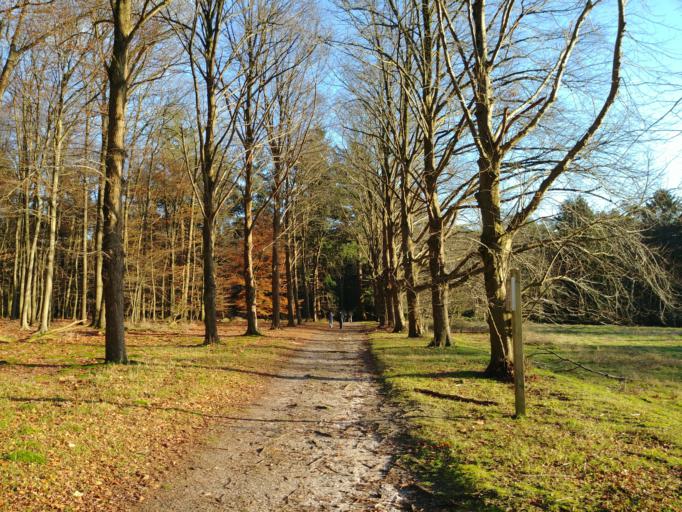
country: NL
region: Utrecht
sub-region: Gemeente Utrechtse Heuvelrug
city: Maarn
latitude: 52.0362
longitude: 5.3790
